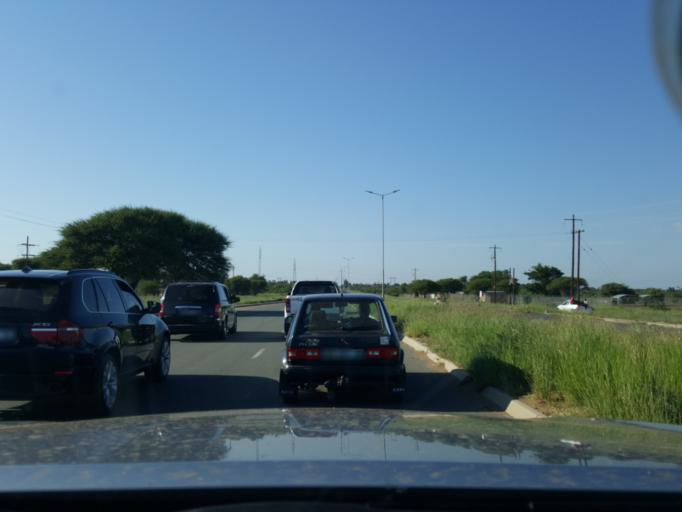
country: ZA
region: North-West
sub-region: Ngaka Modiri Molema District Municipality
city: Mmabatho
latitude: -25.8036
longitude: 25.6319
